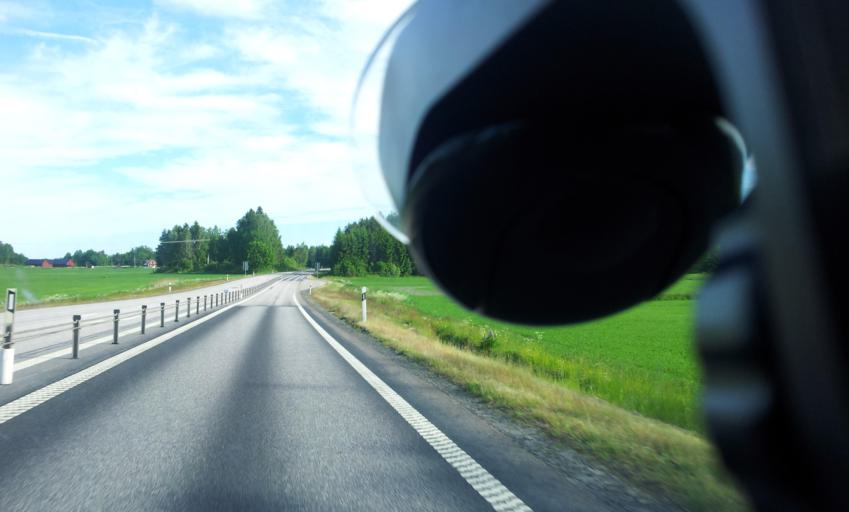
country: SE
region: Kalmar
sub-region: Vasterviks Kommun
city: Forserum
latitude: 58.0677
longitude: 16.5223
